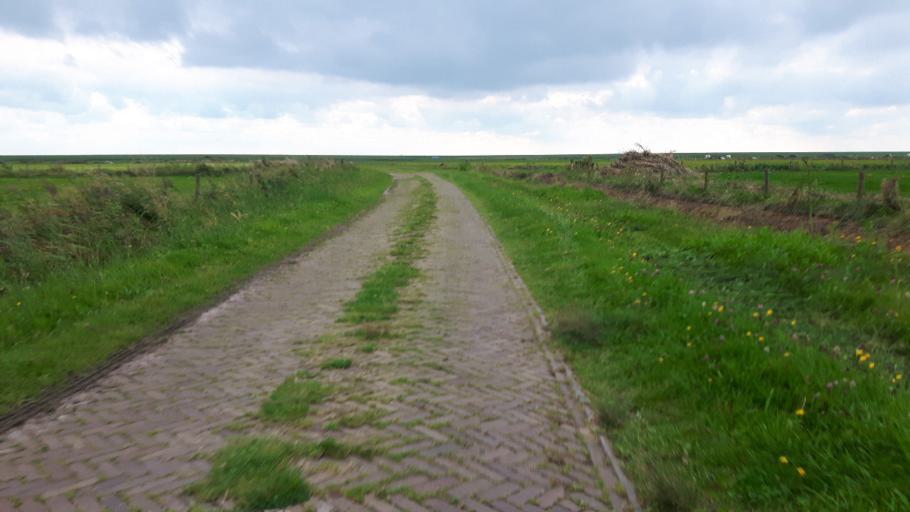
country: NL
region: Friesland
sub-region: Gemeente Ameland
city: Nes
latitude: 53.4471
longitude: 5.8195
